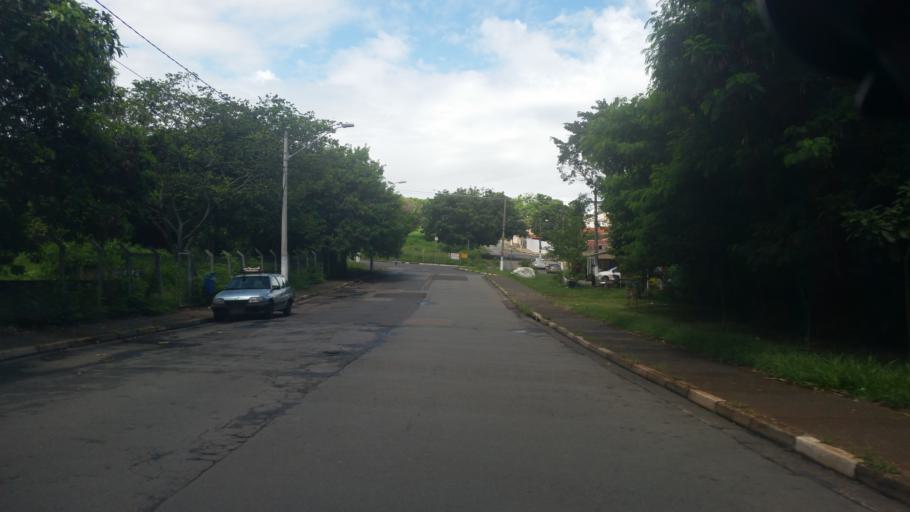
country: BR
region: Sao Paulo
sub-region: Campinas
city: Campinas
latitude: -22.8536
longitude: -47.0608
